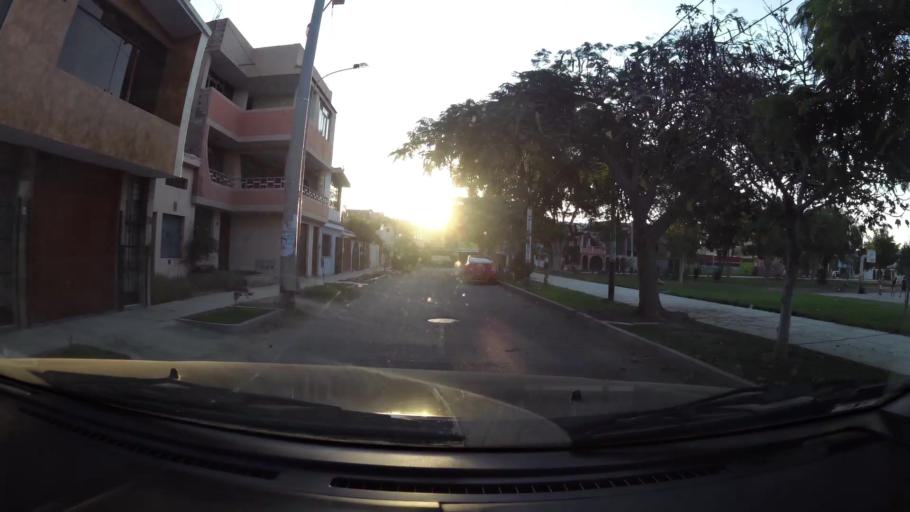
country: PE
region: Ica
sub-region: Provincia de Ica
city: Ica
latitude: -14.0869
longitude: -75.7246
